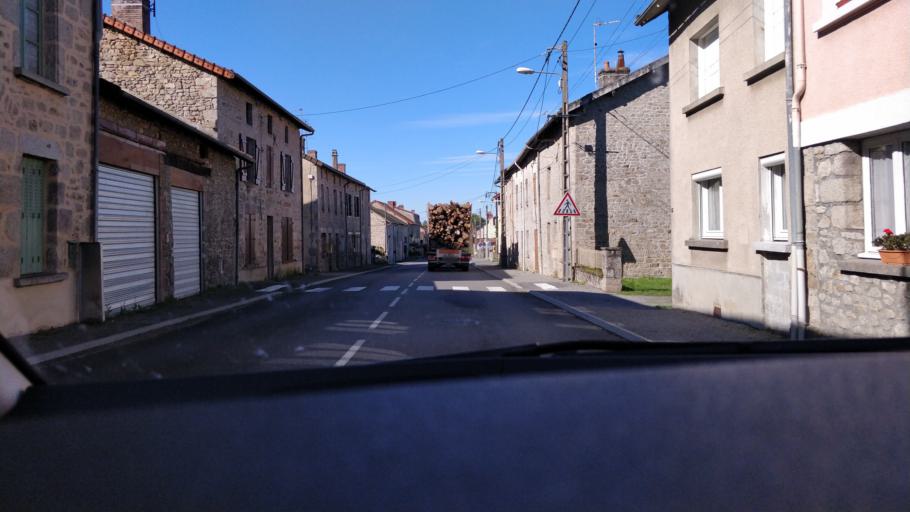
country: FR
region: Limousin
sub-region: Departement de la Haute-Vienne
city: Sauviat-sur-Vige
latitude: 45.9188
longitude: 1.6357
